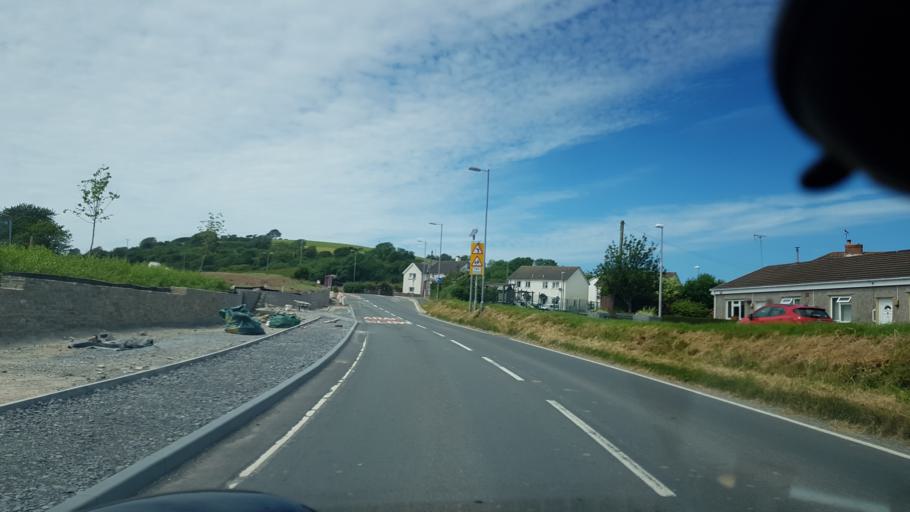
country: GB
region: Wales
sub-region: Carmarthenshire
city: Saint Clears
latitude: 51.7666
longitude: -4.4667
